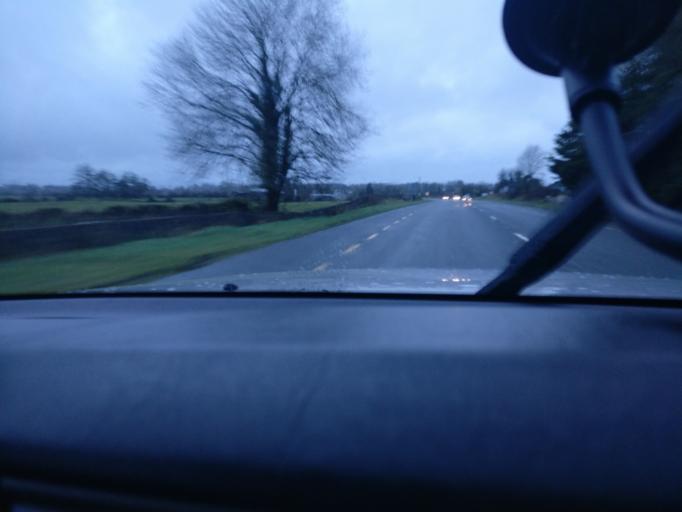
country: IE
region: Connaught
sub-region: County Galway
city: Ballinasloe
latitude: 53.2706
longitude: -8.3940
